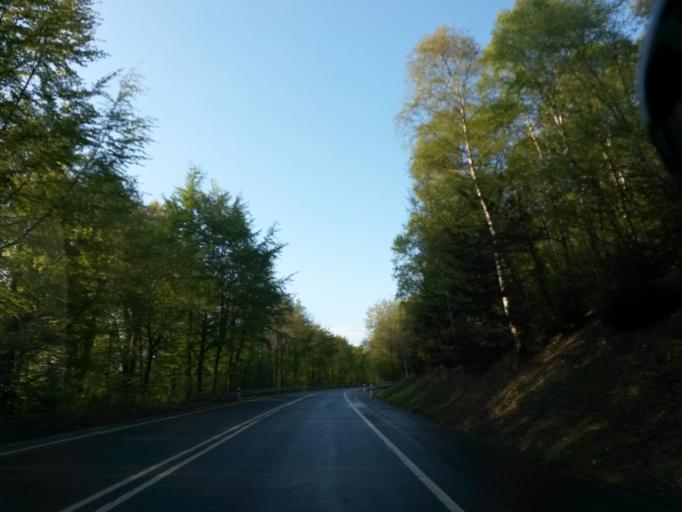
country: DE
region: North Rhine-Westphalia
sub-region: Regierungsbezirk Arnsberg
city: Herscheid
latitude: 51.1303
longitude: 7.7460
